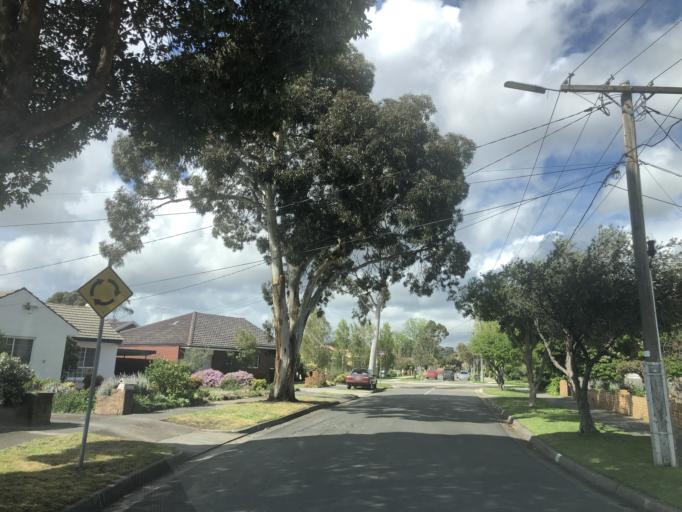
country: AU
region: Victoria
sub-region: Monash
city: Ashwood
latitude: -37.8768
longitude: 145.1206
